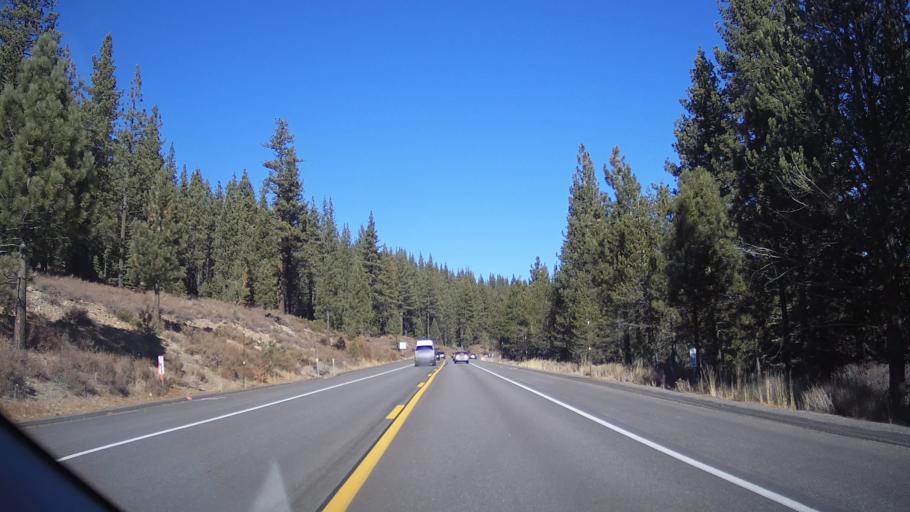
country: US
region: California
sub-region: Nevada County
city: Truckee
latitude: 39.3061
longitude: -120.2060
